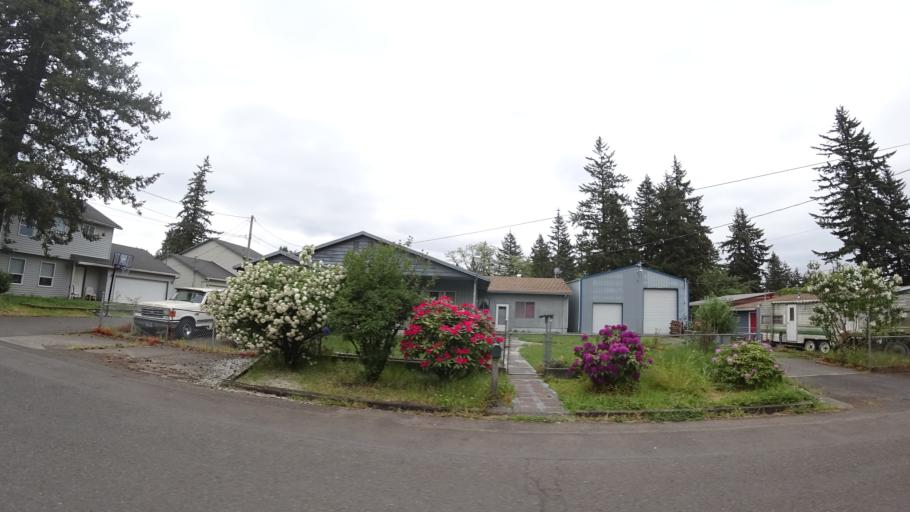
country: US
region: Oregon
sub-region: Multnomah County
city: Lents
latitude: 45.5079
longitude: -122.5189
